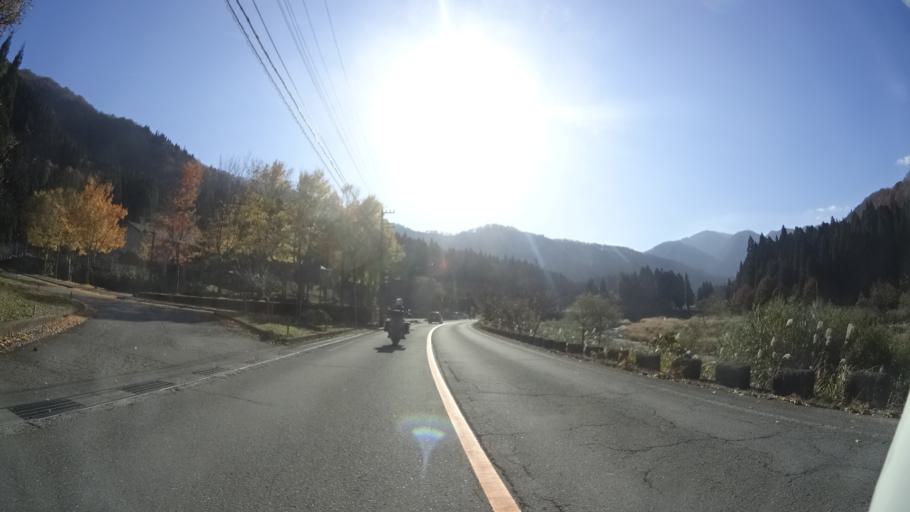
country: JP
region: Fukui
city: Ono
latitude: 35.9234
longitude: 136.6452
